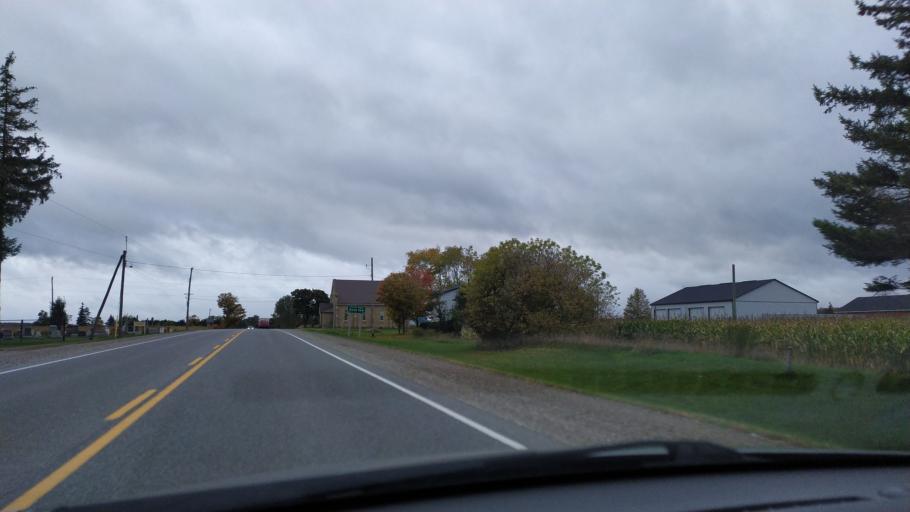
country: CA
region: Ontario
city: Stratford
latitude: 43.3691
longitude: -80.7851
